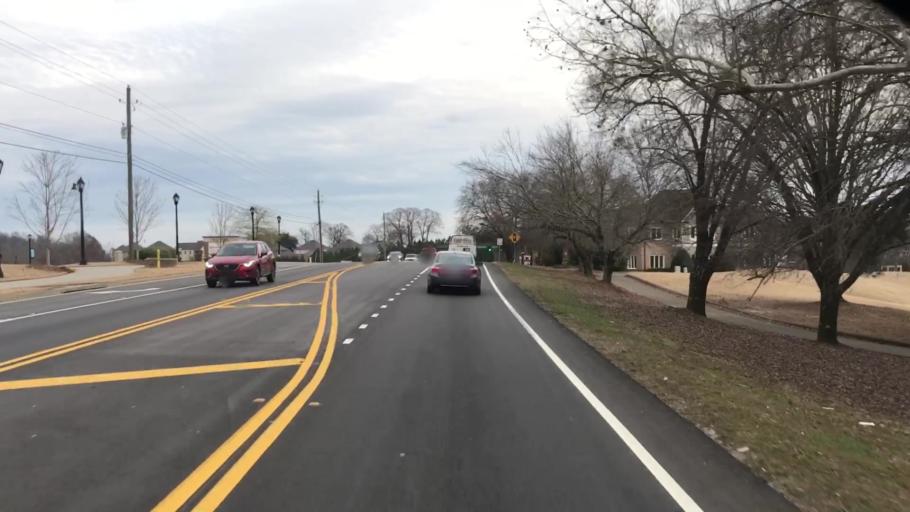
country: US
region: Georgia
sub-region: Jackson County
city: Braselton
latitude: 34.1145
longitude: -83.8210
